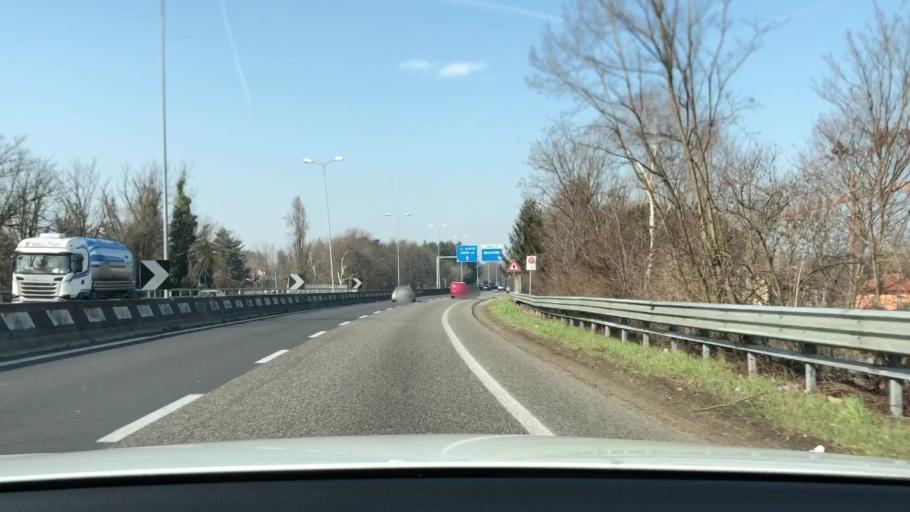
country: IT
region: Lombardy
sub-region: Provincia di Monza e Brianza
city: Barlassina
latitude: 45.6579
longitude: 9.1369
